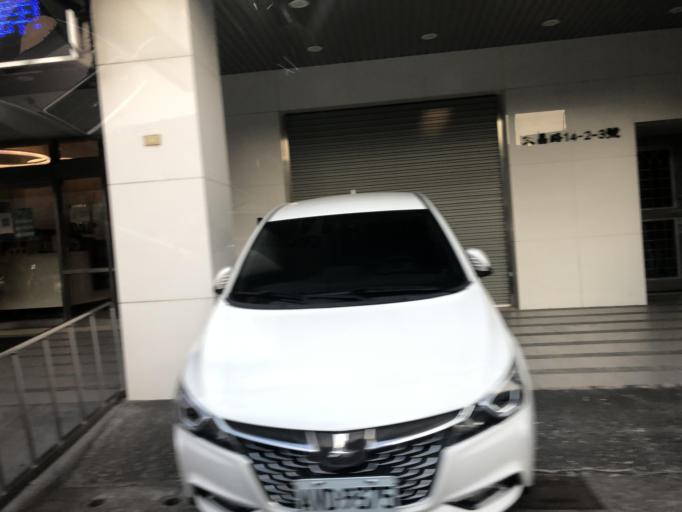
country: TW
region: Taiwan
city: Xinying
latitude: 23.1848
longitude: 120.2522
